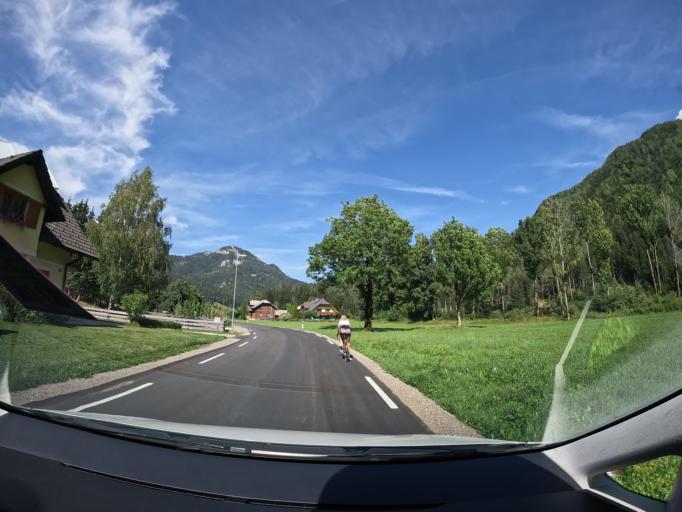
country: AT
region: Carinthia
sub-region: Politischer Bezirk Feldkirchen
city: Feldkirchen in Karnten
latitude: 46.6883
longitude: 14.1198
